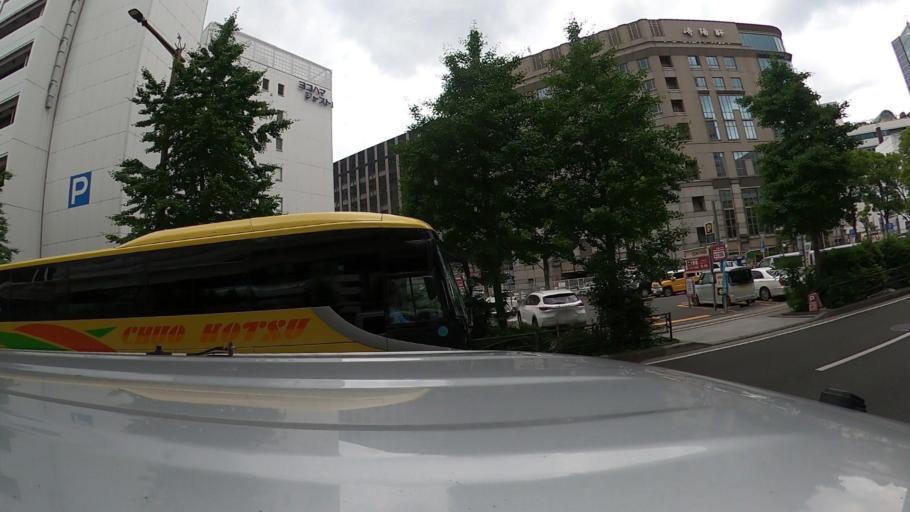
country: JP
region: Kanagawa
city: Yokohama
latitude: 35.4634
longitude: 139.6237
